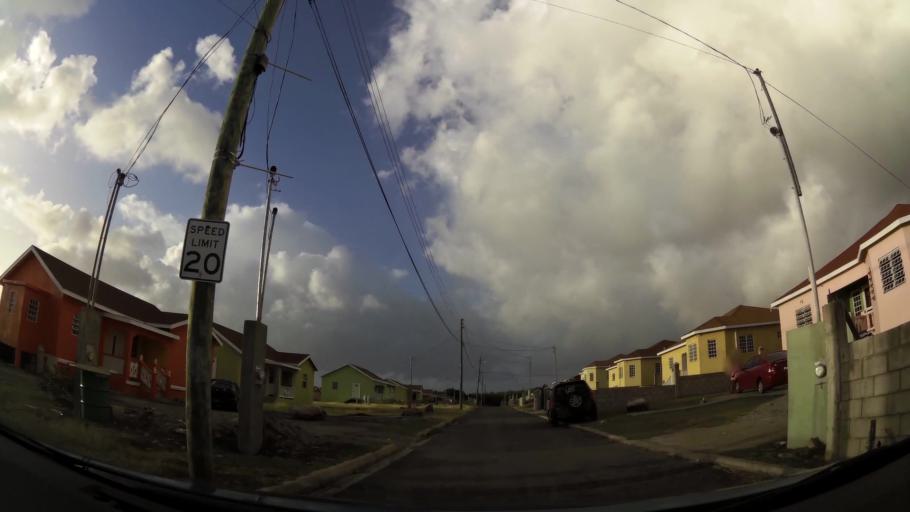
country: KN
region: Saint John Figtree
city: Fig Tree
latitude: 17.1171
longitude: -62.6154
